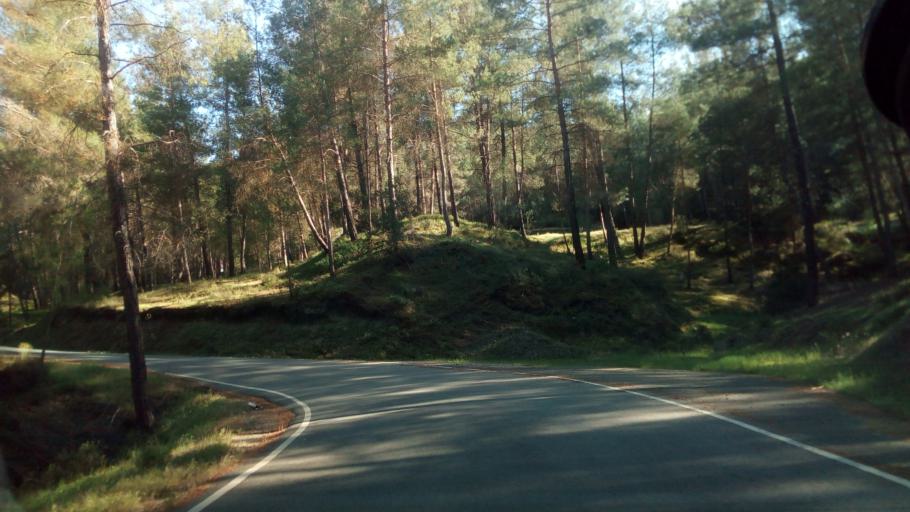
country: CY
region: Limassol
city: Pachna
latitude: 34.8852
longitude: 32.7550
